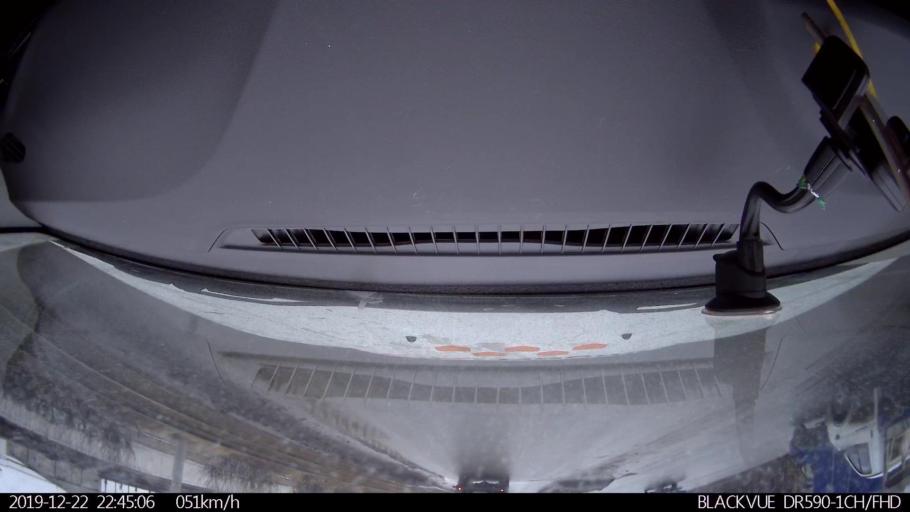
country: RU
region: Nizjnij Novgorod
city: Nizhniy Novgorod
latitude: 56.2705
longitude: 43.9104
